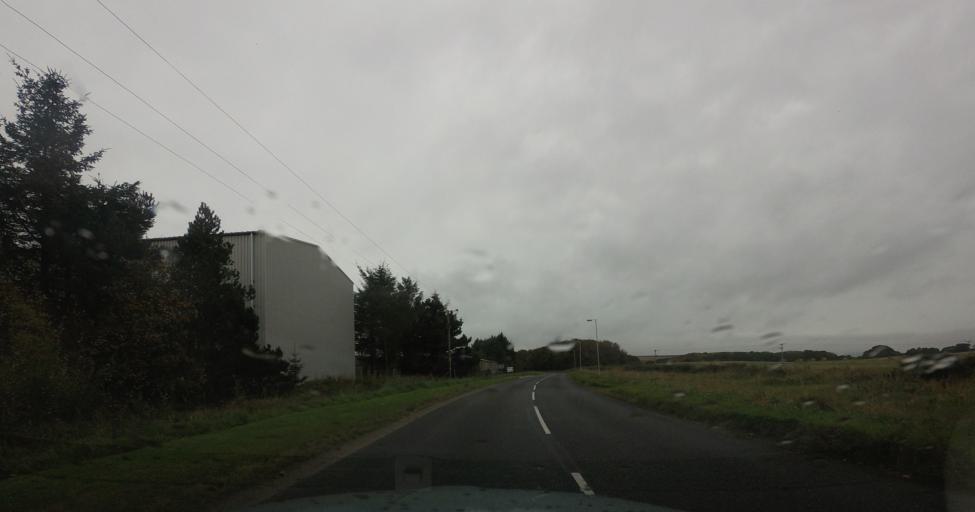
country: GB
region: Scotland
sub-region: Aberdeenshire
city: Whitehills
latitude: 57.6689
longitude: -2.5648
